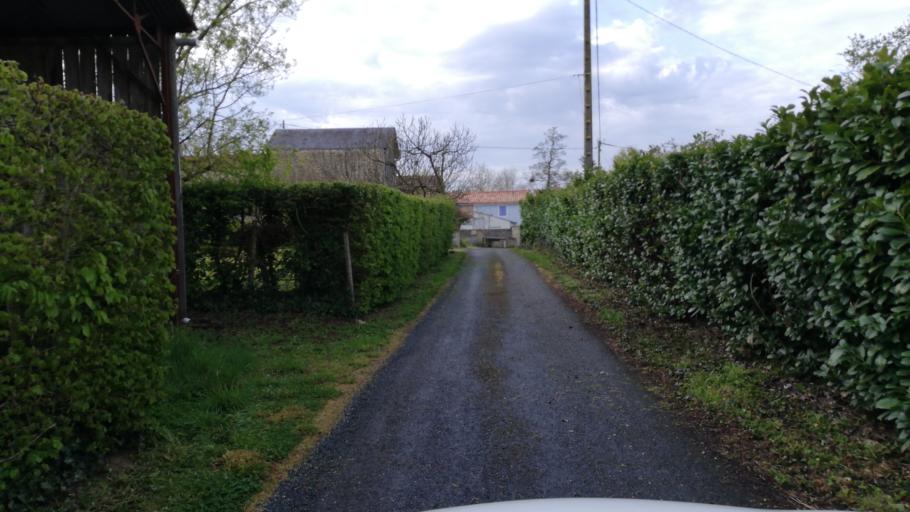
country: FR
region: Pays de la Loire
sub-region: Departement de la Vendee
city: Maillezais
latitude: 46.3240
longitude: -0.7142
